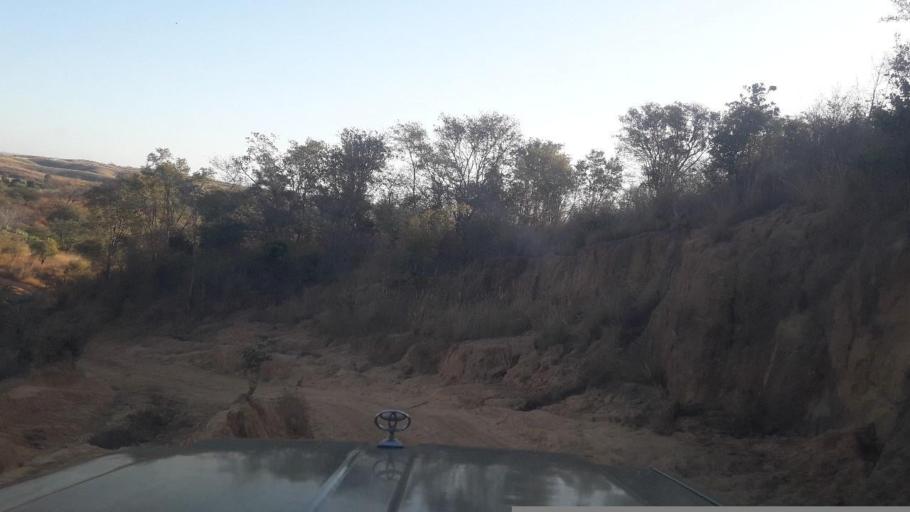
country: MG
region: Boeny
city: Sitampiky
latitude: -16.5039
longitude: 45.6014
